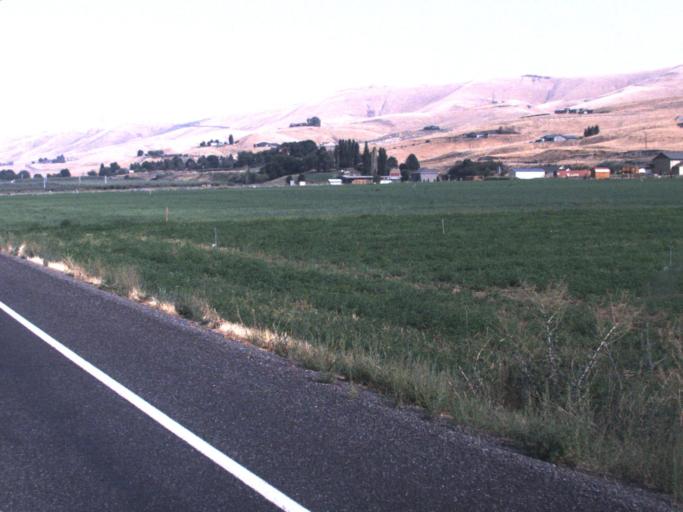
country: US
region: Washington
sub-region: Benton County
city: Prosser
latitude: 46.1885
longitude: -119.8322
